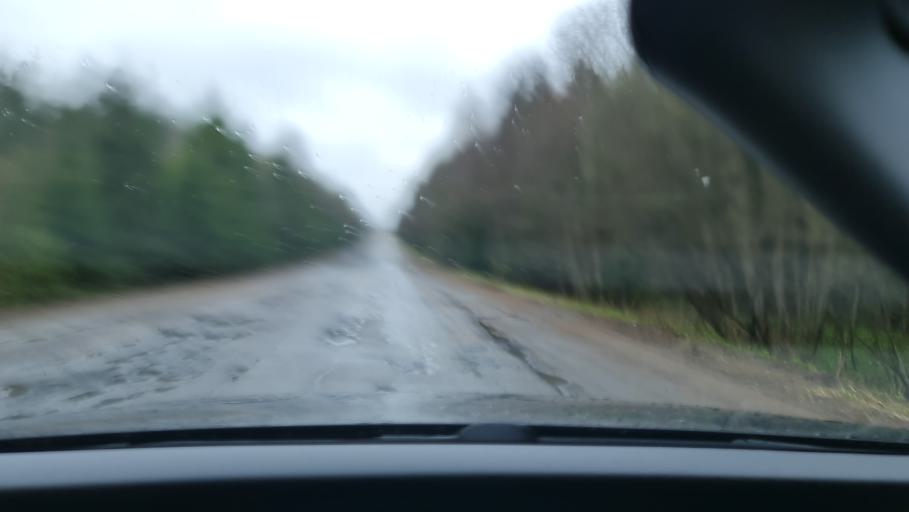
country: RU
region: Novgorod
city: Valday
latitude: 58.0353
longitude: 32.8635
